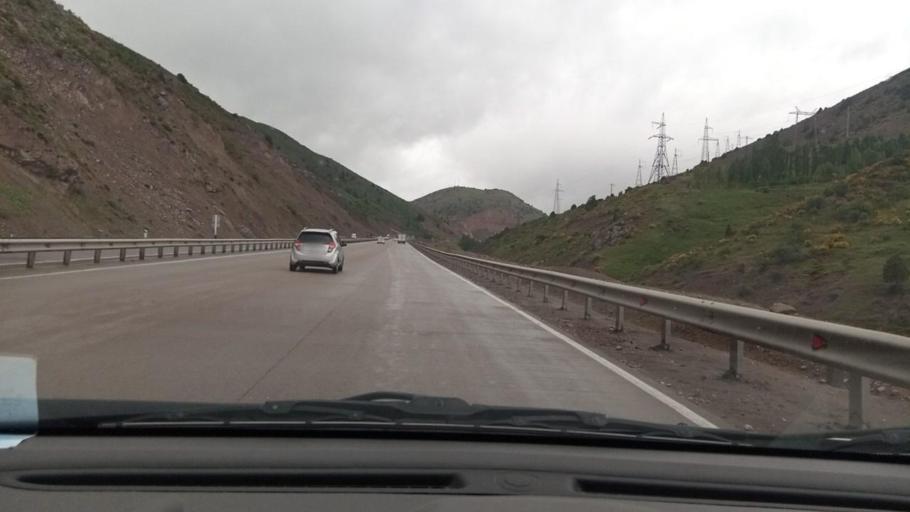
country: UZ
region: Toshkent
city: Angren
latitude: 41.0542
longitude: 70.5658
